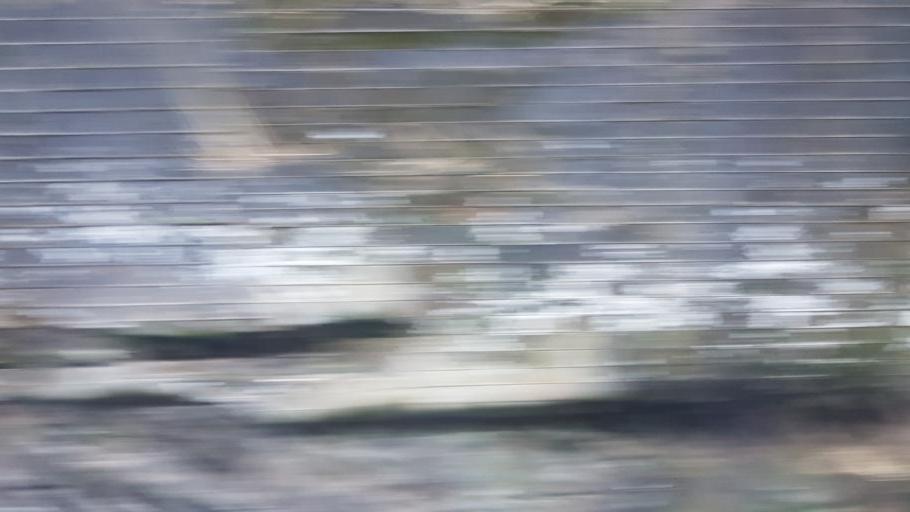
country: FR
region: Lorraine
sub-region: Departement des Vosges
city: Xertigny
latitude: 48.0710
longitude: 6.4175
